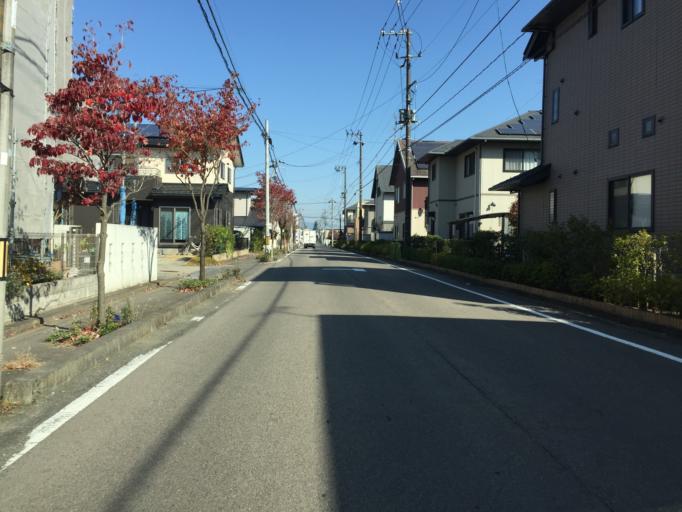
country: JP
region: Fukushima
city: Fukushima-shi
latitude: 37.7689
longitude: 140.4873
